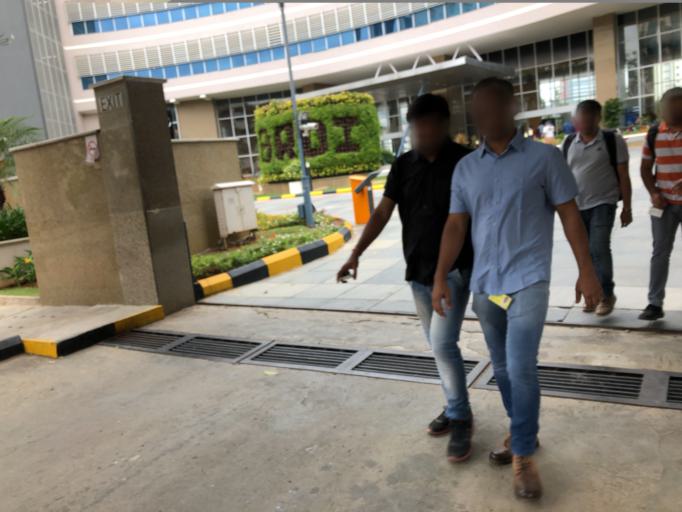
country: IN
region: Karnataka
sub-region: Bangalore Rural
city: Hoskote
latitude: 12.9853
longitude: 77.7273
